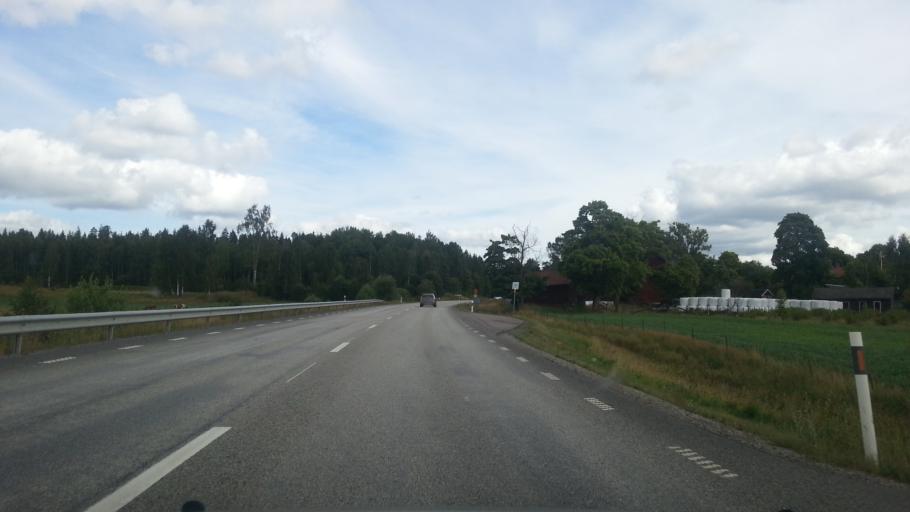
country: SE
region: OErebro
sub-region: Lindesbergs Kommun
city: Lindesberg
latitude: 59.6454
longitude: 15.2356
